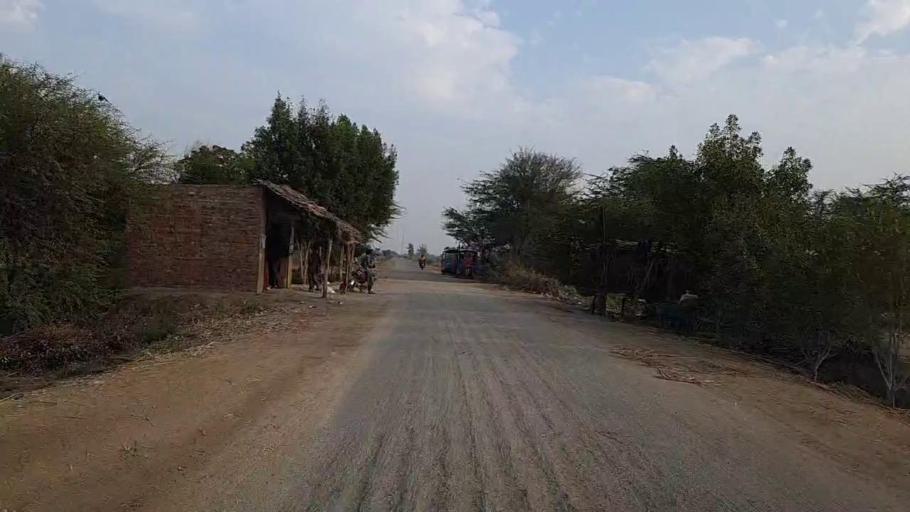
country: PK
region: Sindh
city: Samaro
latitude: 25.3896
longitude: 69.3246
